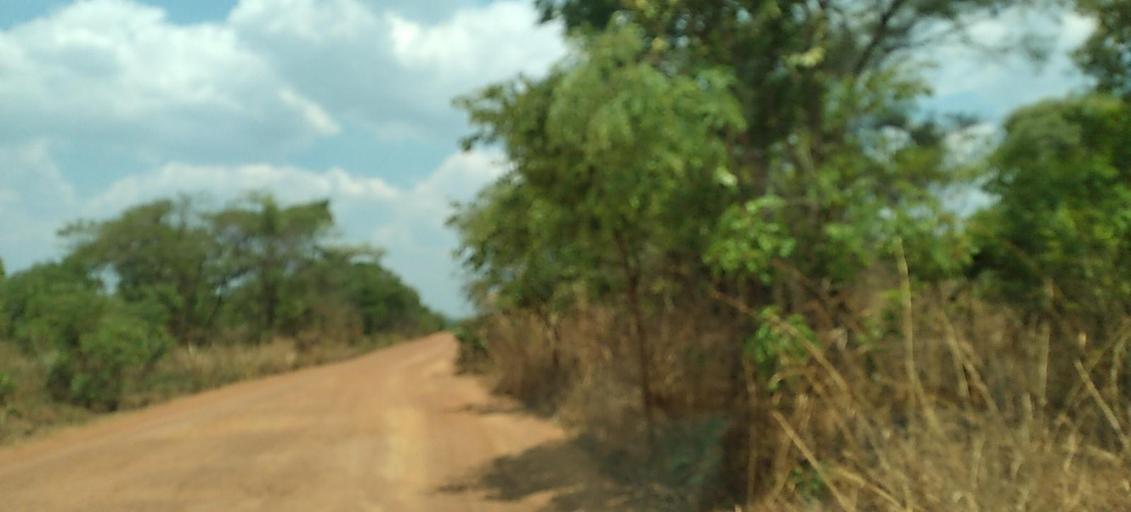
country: ZM
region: Copperbelt
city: Luanshya
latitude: -13.3835
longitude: 28.4392
